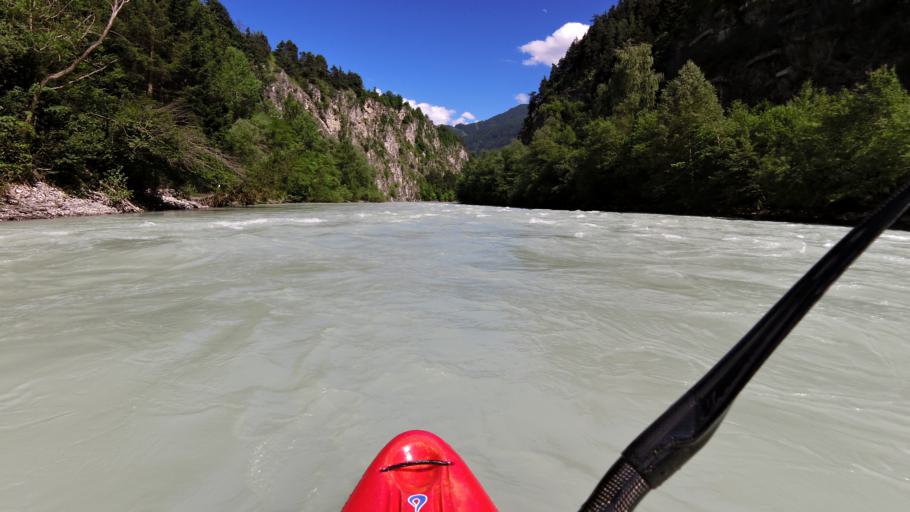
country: AT
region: Tyrol
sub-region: Politischer Bezirk Imst
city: Karrosten
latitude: 47.2170
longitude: 10.7705
